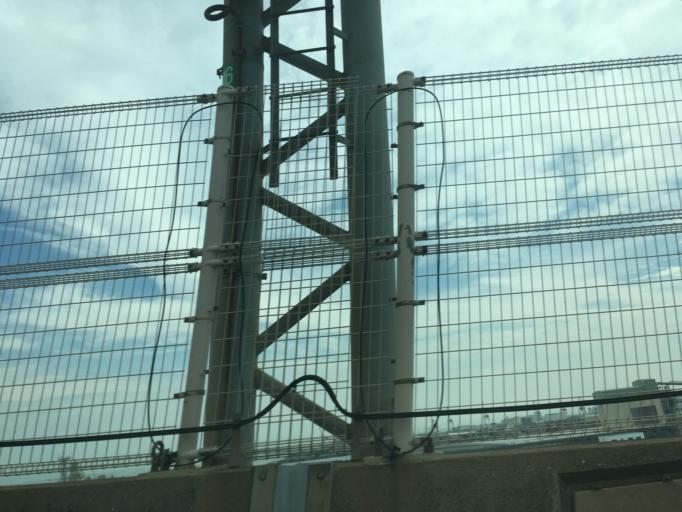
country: JP
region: Hyogo
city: Ashiya
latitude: 34.7082
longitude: 135.2840
